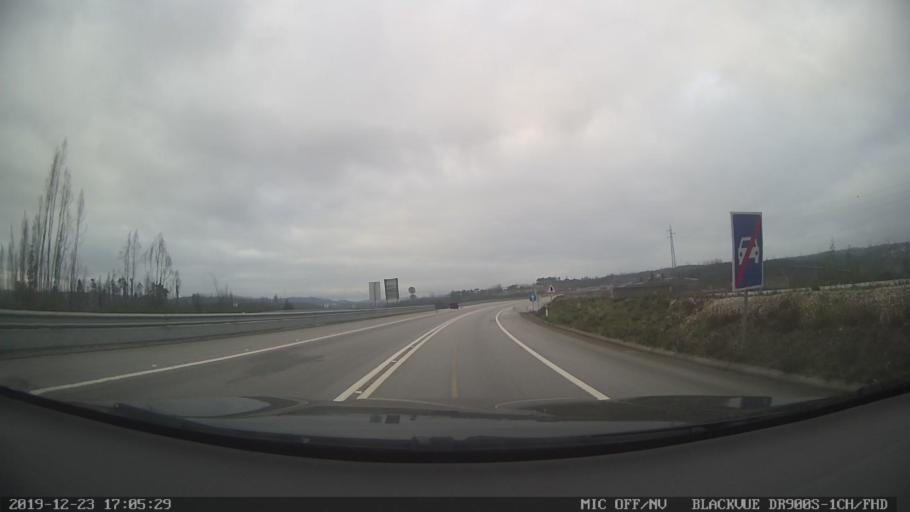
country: PT
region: Viseu
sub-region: Santa Comba Dao
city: Santa Comba Dao
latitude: 40.3471
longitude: -8.1764
